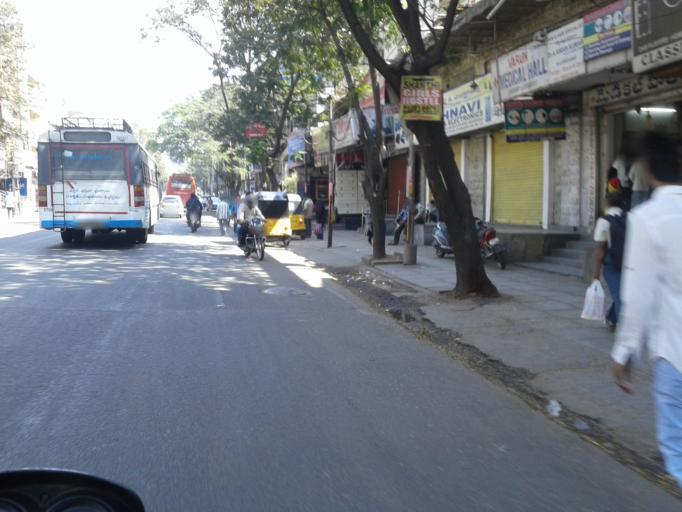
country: IN
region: Telangana
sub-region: Hyderabad
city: Hyderabad
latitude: 17.3853
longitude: 78.4822
